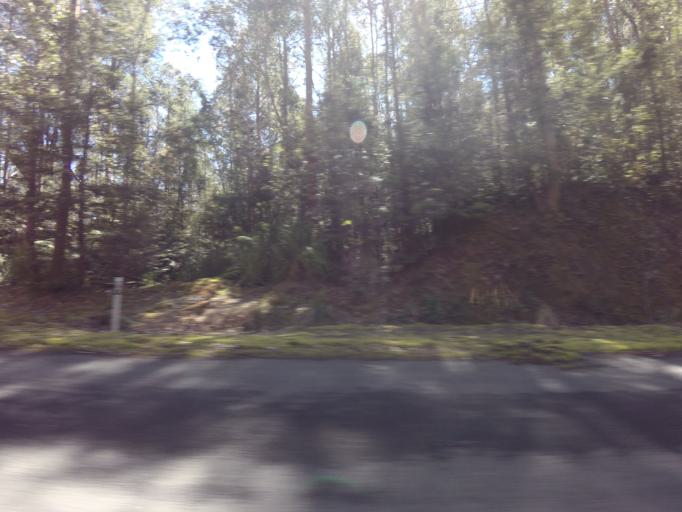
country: AU
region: Tasmania
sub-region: Huon Valley
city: Geeveston
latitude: -42.8189
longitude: 146.3078
